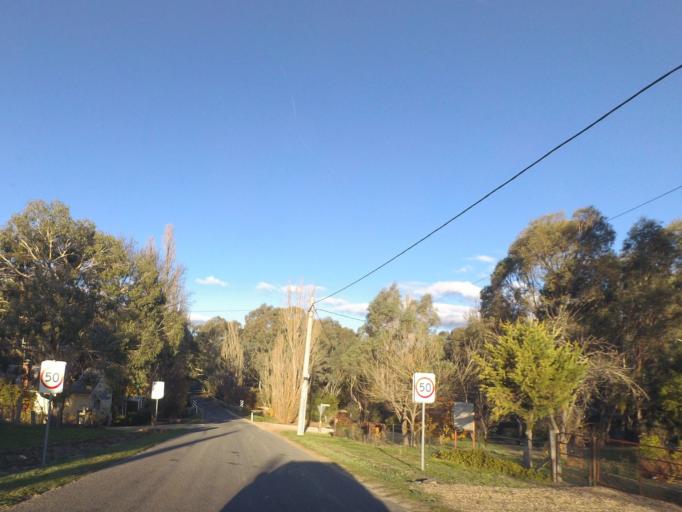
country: AU
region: Victoria
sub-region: Mount Alexander
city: Castlemaine
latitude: -37.1565
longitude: 144.2083
